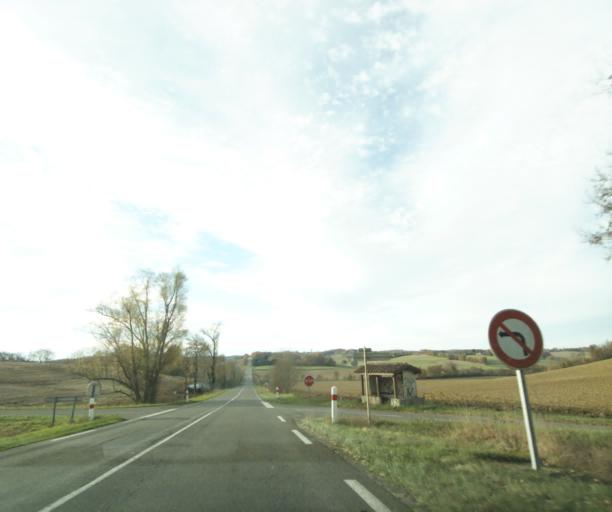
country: FR
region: Midi-Pyrenees
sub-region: Departement du Gers
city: Vic-Fezensac
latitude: 43.7573
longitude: 0.2331
